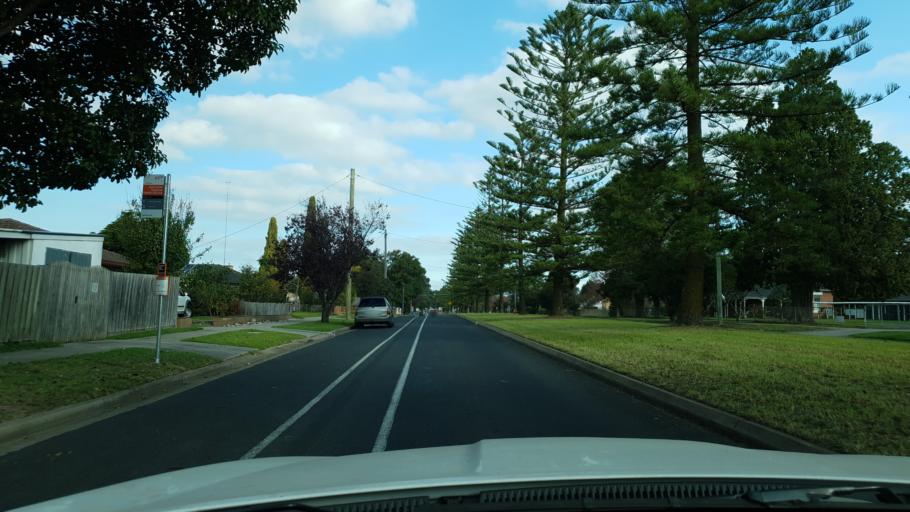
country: AU
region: Victoria
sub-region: East Gippsland
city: Bairnsdale
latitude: -37.8202
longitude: 147.6083
